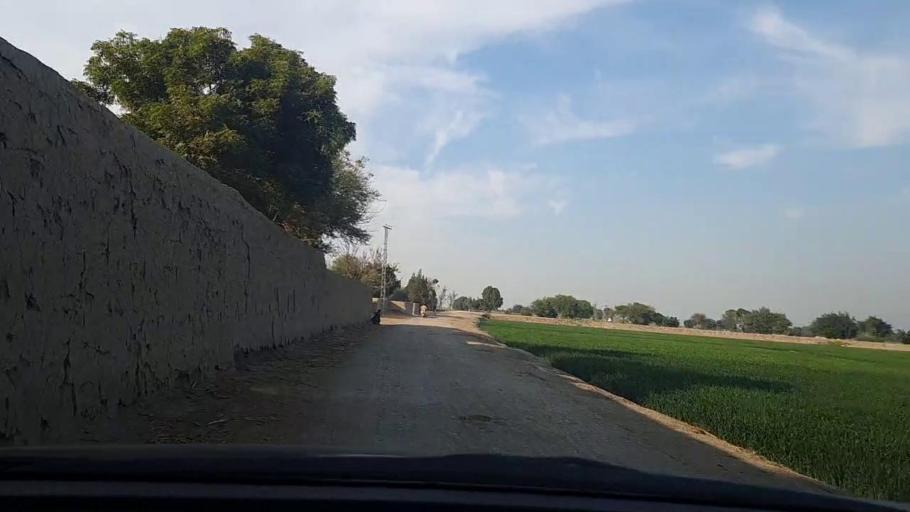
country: PK
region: Sindh
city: Daulatpur
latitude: 26.3196
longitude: 68.0204
